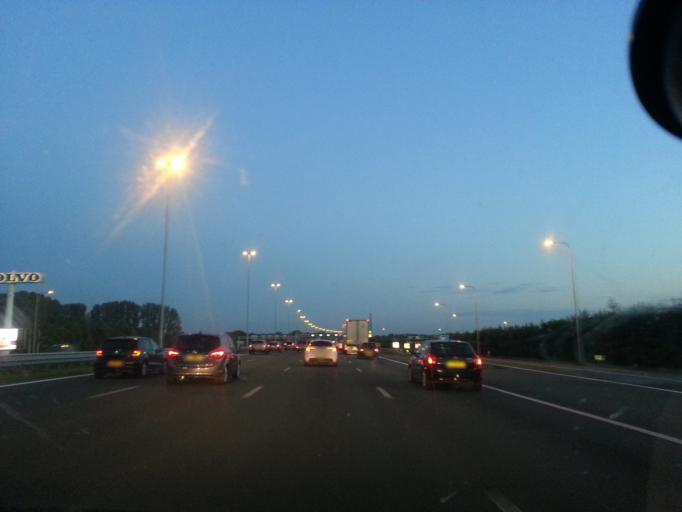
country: NL
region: Gelderland
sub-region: Gemeente Culemborg
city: Culemborg
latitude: 51.8987
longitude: 5.1903
